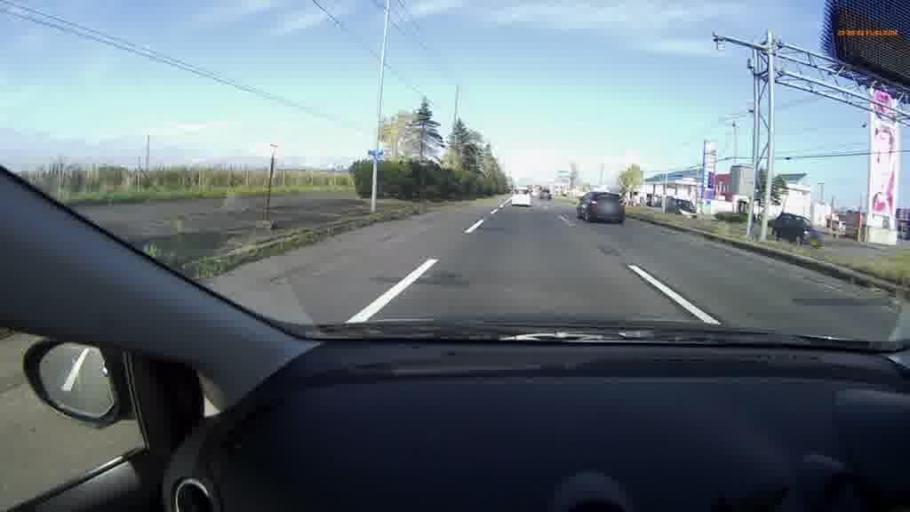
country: JP
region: Hokkaido
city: Kushiro
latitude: 43.0067
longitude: 144.4146
